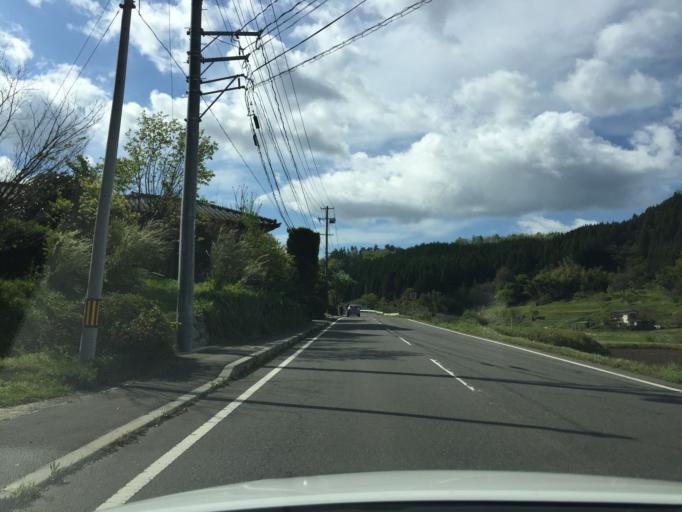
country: JP
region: Fukushima
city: Fukushima-shi
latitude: 37.6493
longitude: 140.6129
